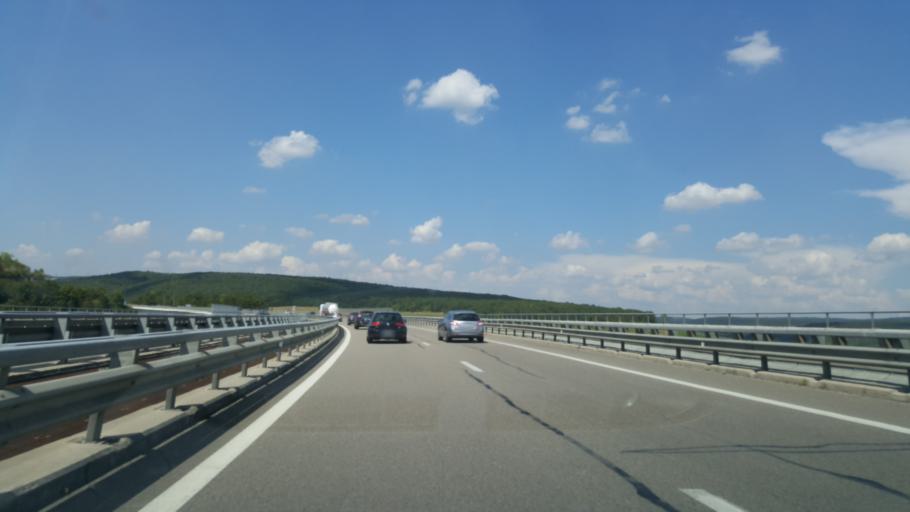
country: FR
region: Bourgogne
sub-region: Departement de la Cote-d'Or
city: Savigny-les-Beaune
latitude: 47.1633
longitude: 4.6984
